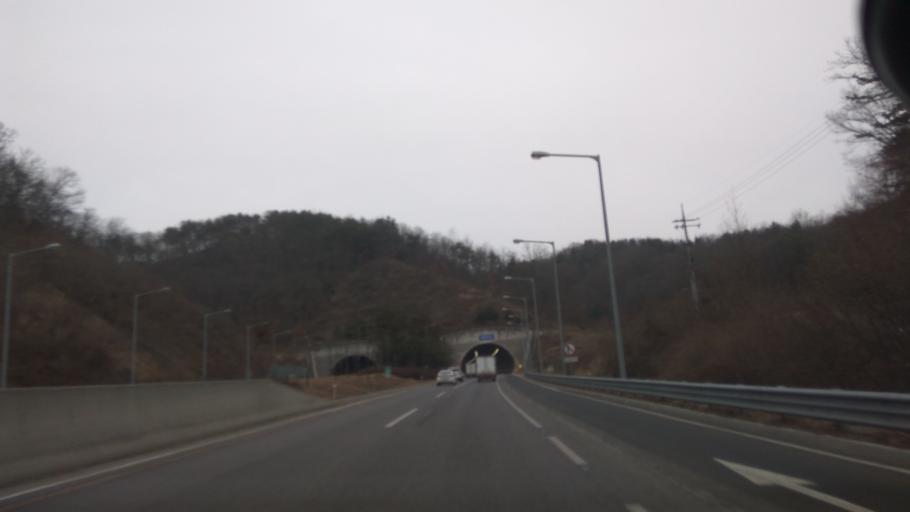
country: KR
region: Gangwon-do
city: Sindong
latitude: 37.7462
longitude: 127.6981
